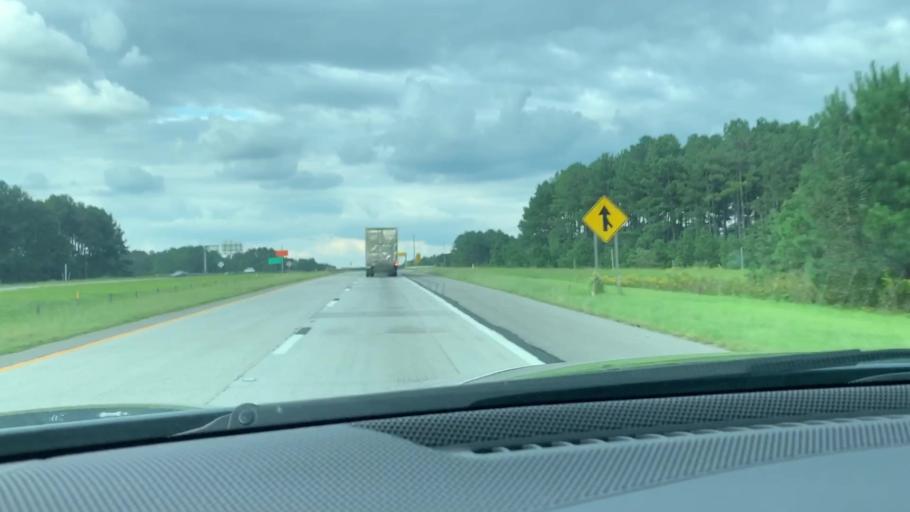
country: US
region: South Carolina
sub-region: Dorchester County
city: Saint George
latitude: 33.3163
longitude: -80.5494
